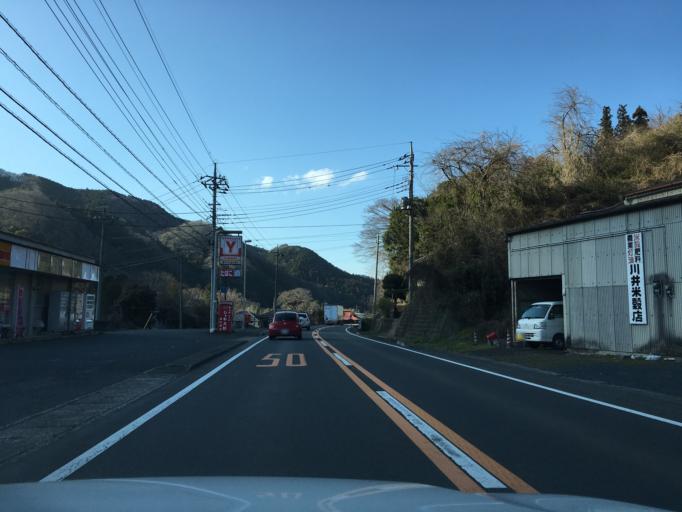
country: JP
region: Ibaraki
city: Daigo
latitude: 36.6984
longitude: 140.3849
